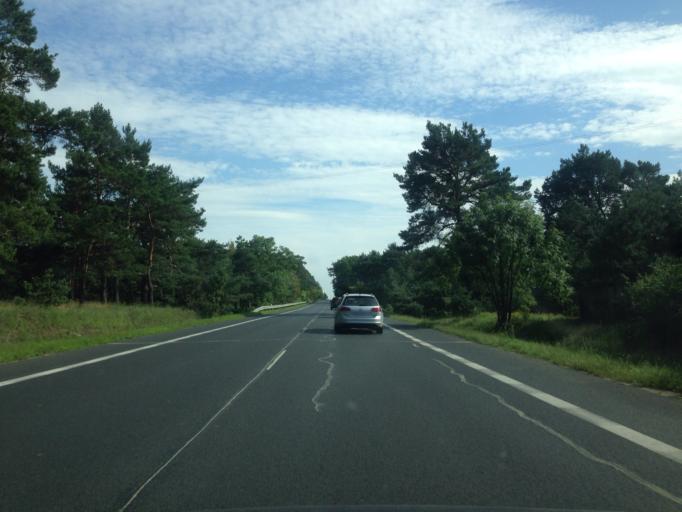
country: PL
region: Kujawsko-Pomorskie
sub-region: Powiat aleksandrowski
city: Aleksandrow Kujawski
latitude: 52.9500
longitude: 18.6934
